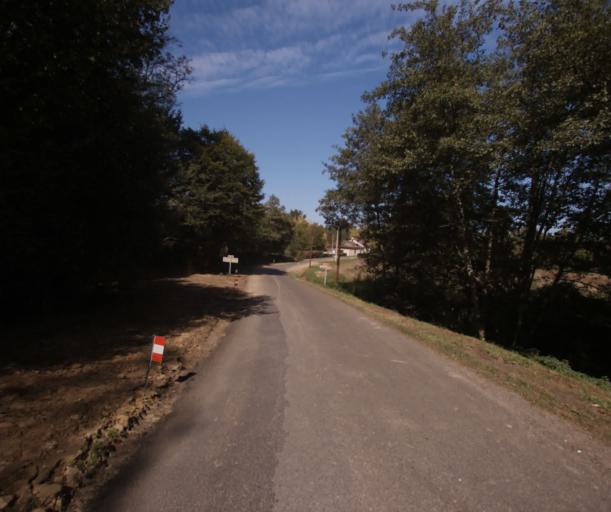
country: FR
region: Midi-Pyrenees
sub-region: Departement du Gers
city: Cazaubon
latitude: 43.9431
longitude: -0.0716
